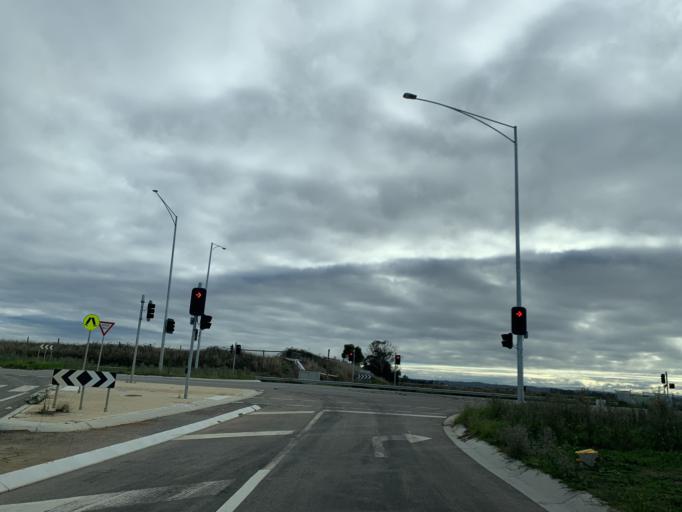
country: AU
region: Victoria
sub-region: Cardinia
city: Officer South
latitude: -38.1237
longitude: 145.3647
